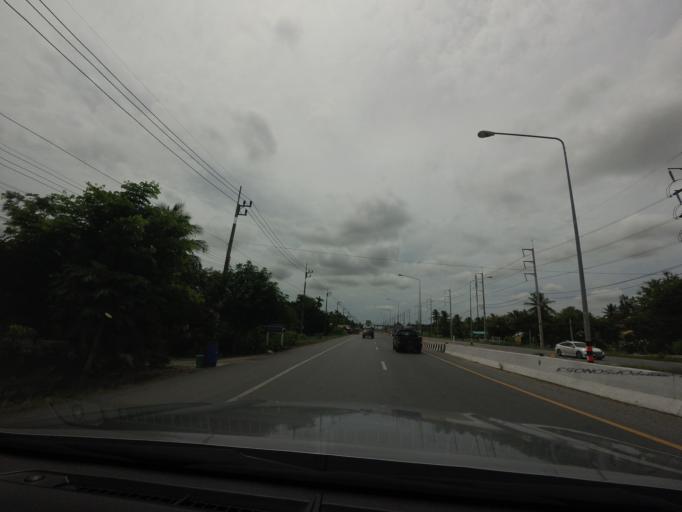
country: TH
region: Nakhon Si Thammarat
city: Hua Sai
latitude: 8.0514
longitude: 100.2133
